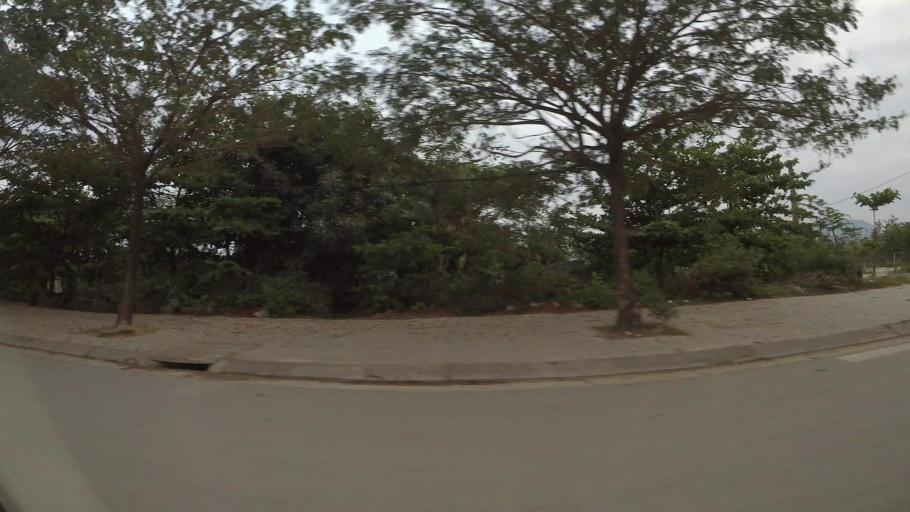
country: VN
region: Da Nang
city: Lien Chieu
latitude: 16.1082
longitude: 108.1286
